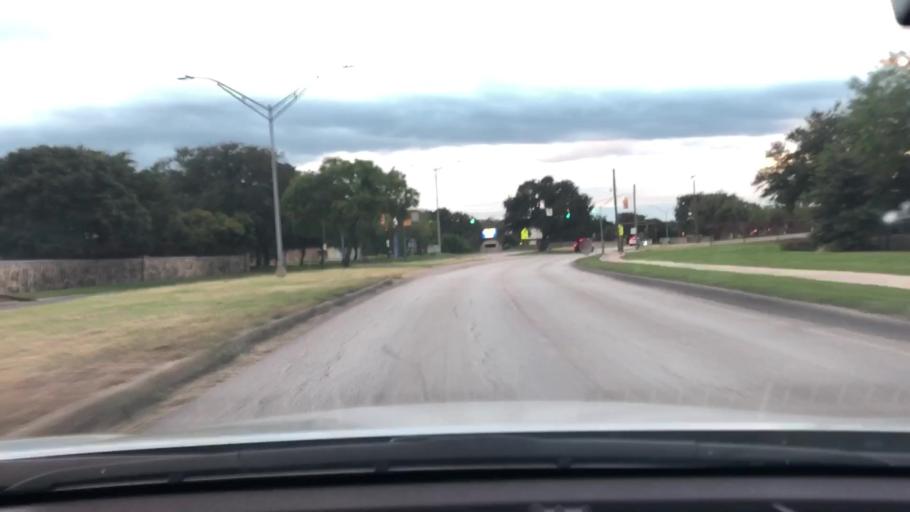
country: US
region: Texas
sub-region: Bexar County
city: Shavano Park
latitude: 29.5881
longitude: -98.5297
